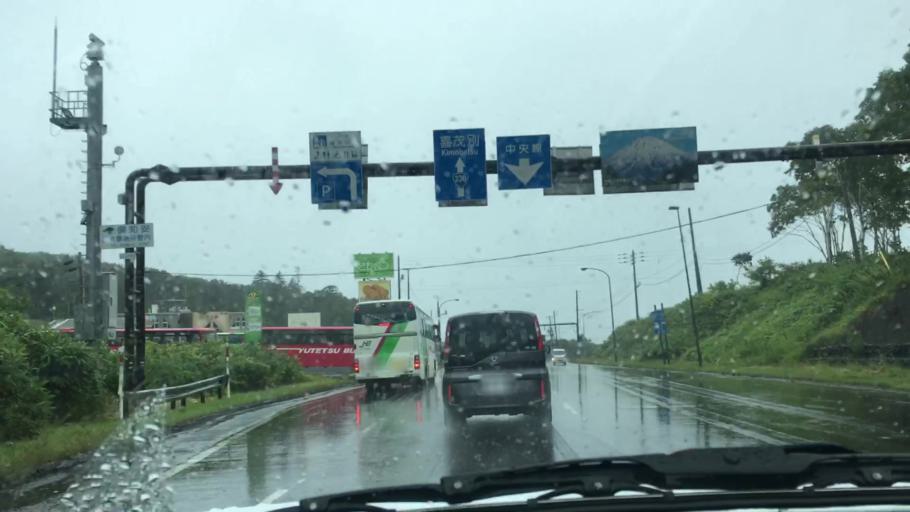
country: JP
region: Hokkaido
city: Sapporo
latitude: 42.8575
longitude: 141.0987
